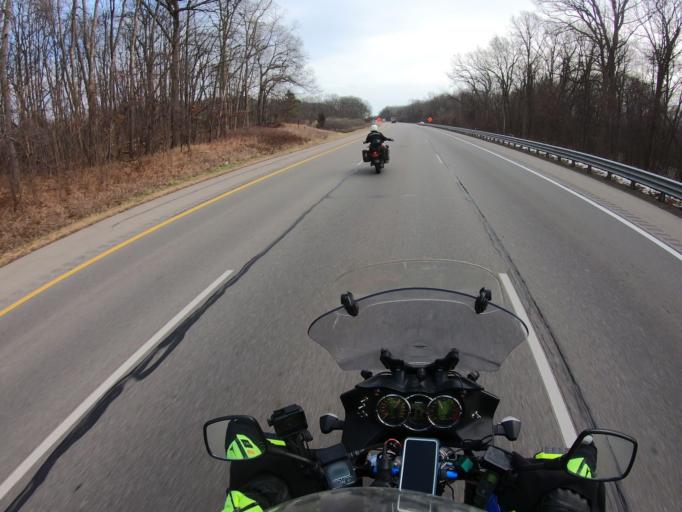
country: US
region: Michigan
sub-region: Oakland County
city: Clarkston
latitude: 42.7464
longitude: -83.4952
